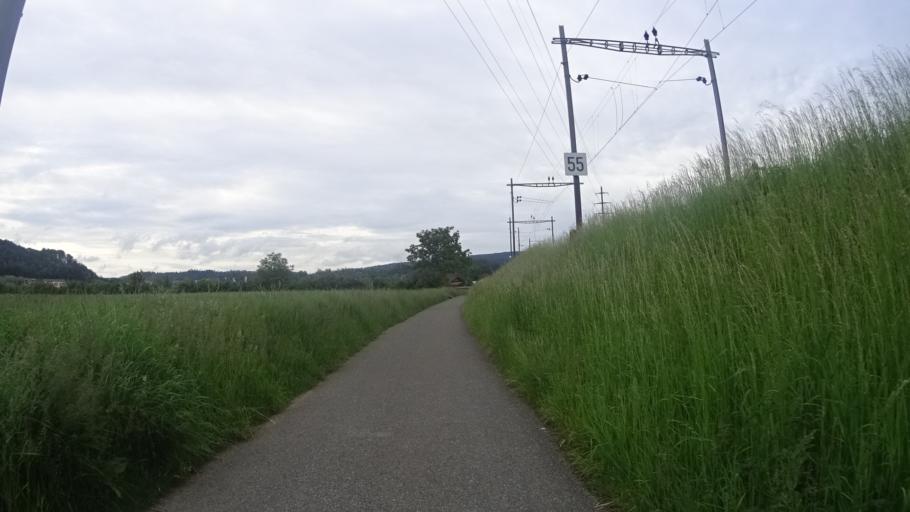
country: DE
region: Baden-Wuerttemberg
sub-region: Freiburg Region
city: Waldshut-Tiengen
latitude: 47.6098
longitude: 8.2176
